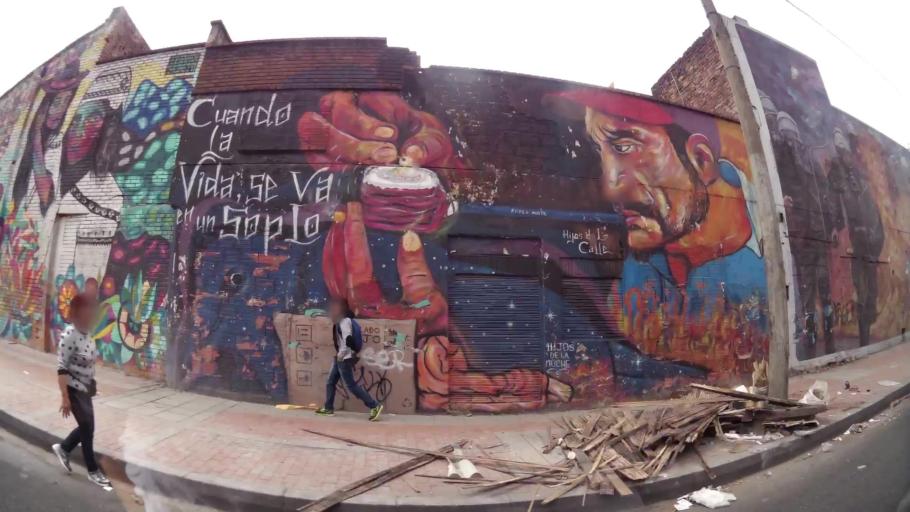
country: CO
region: Bogota D.C.
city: Bogota
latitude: 4.6169
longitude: -74.0769
